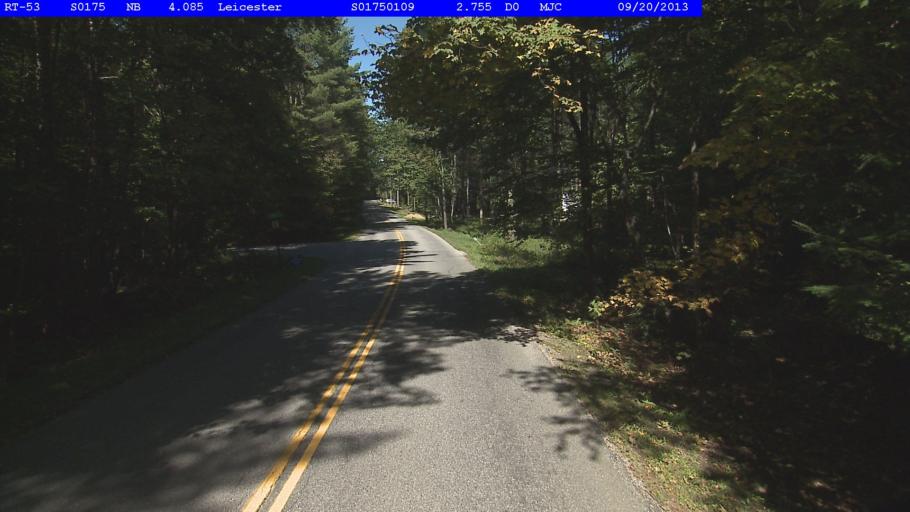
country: US
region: Vermont
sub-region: Rutland County
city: Brandon
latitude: 43.8824
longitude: -73.0635
